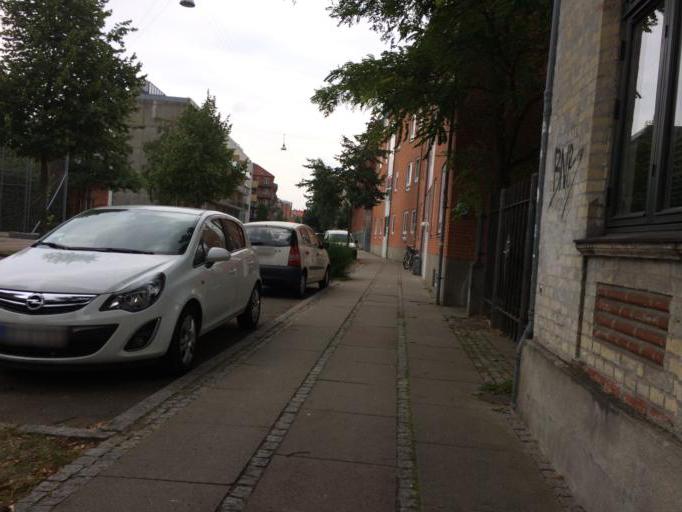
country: DK
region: Capital Region
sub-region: Kobenhavn
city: Christianshavn
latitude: 55.6612
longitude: 12.6074
